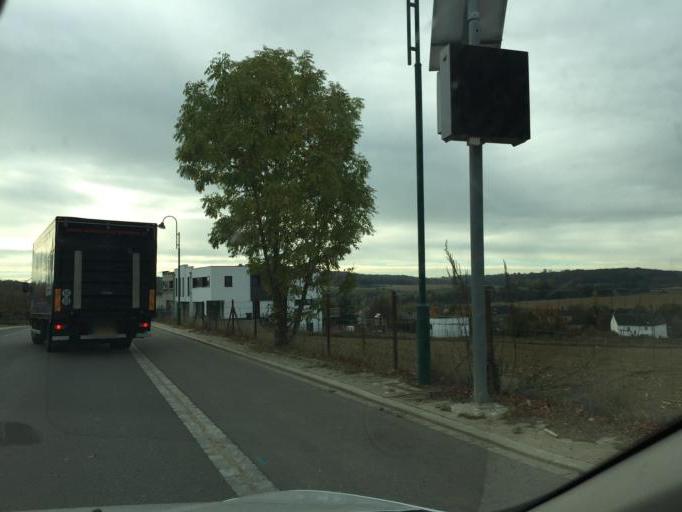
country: LU
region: Luxembourg
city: Capellen
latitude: 49.6188
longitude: 5.9841
